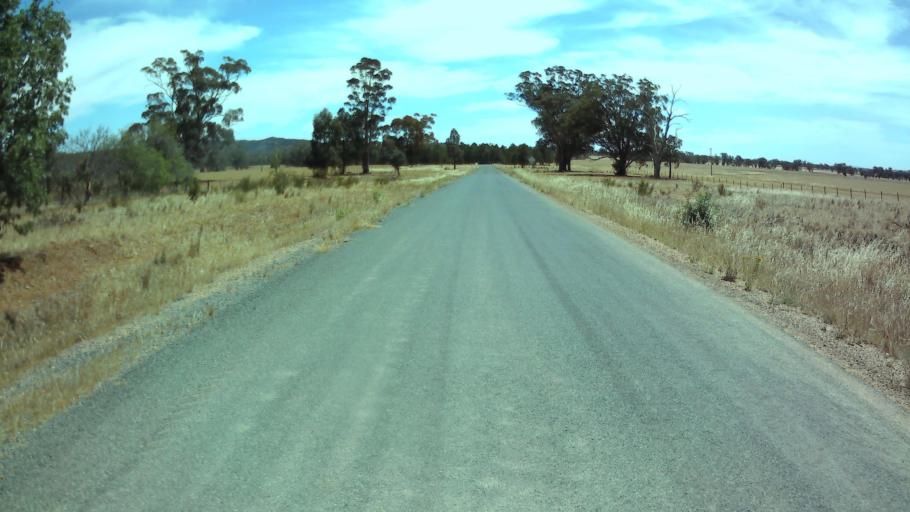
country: AU
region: New South Wales
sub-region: Weddin
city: Grenfell
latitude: -33.7751
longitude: 148.2073
